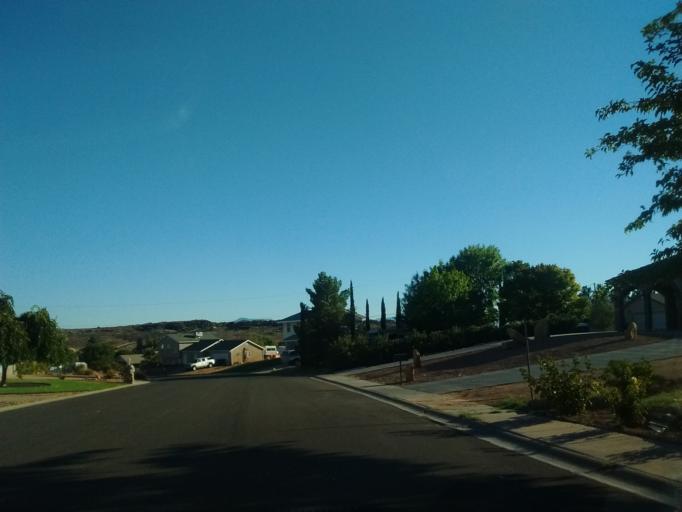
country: US
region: Utah
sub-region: Washington County
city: Washington
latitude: 37.1349
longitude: -113.4996
